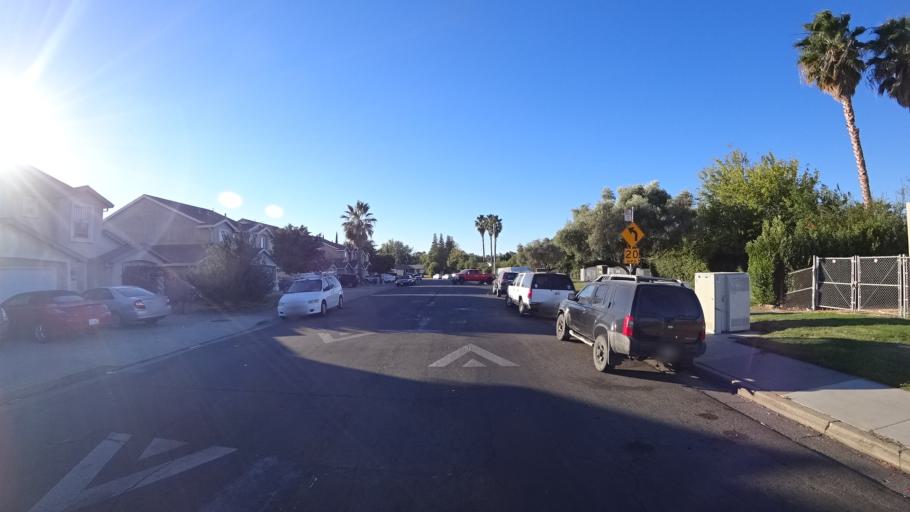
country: US
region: California
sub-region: Sacramento County
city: Parkway
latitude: 38.4925
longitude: -121.4644
